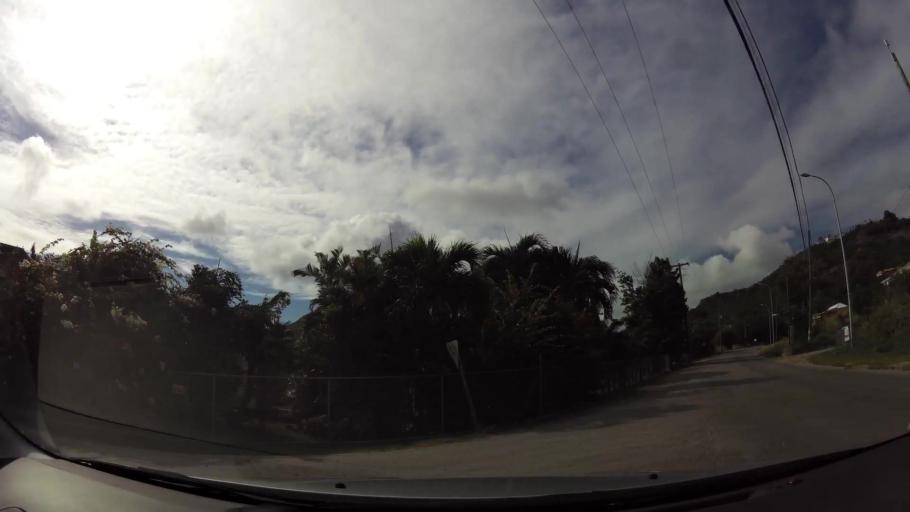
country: AG
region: Saint Paul
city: Falmouth
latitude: 17.0256
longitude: -61.7802
